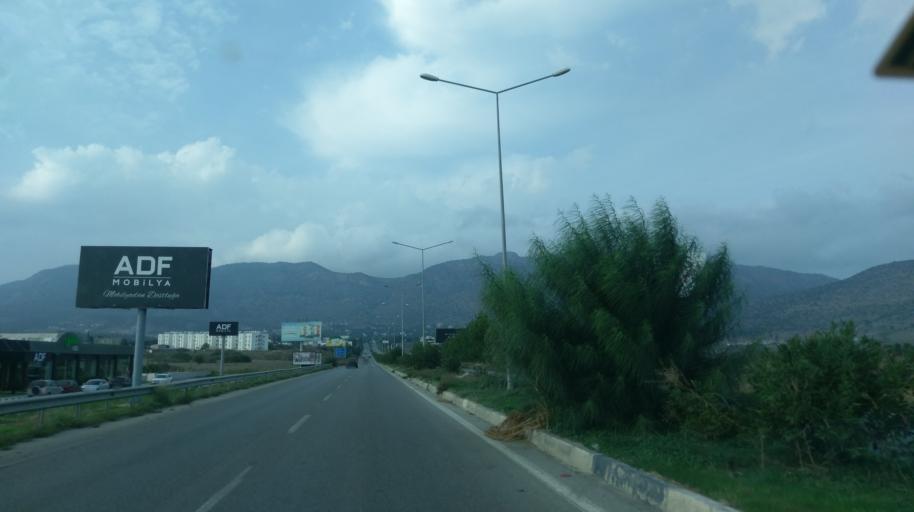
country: CY
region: Keryneia
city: Kyrenia
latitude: 35.2740
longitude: 33.2874
